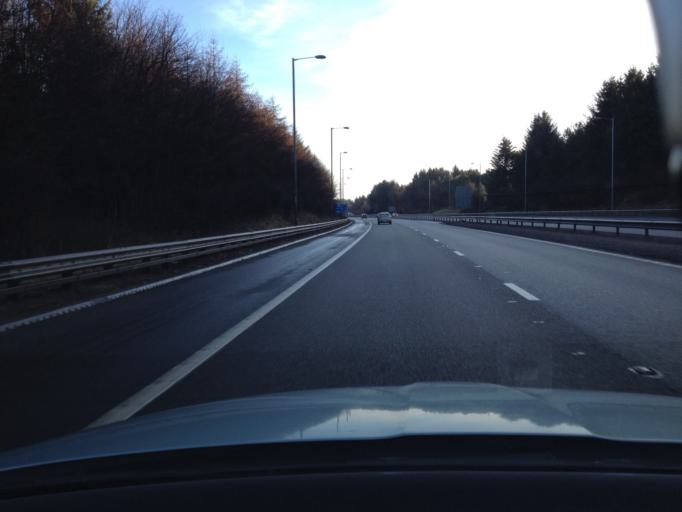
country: GB
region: Scotland
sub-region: West Lothian
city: Livingston
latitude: 55.9166
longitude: -3.5188
